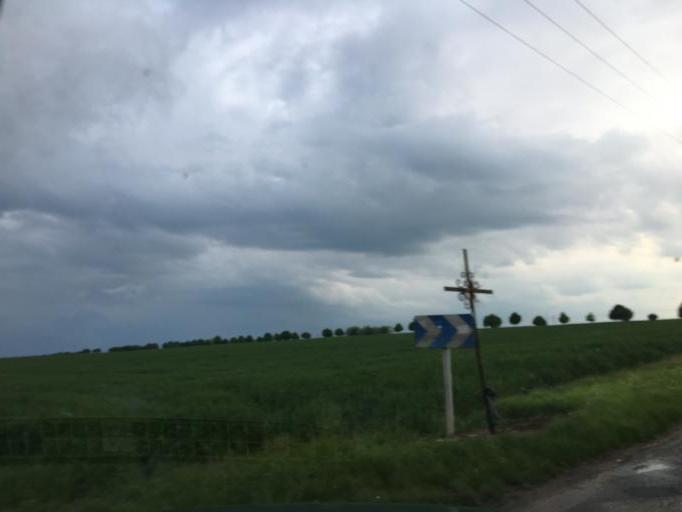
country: FR
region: Centre
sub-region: Departement du Loiret
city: Tavers
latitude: 47.7588
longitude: 1.6046
